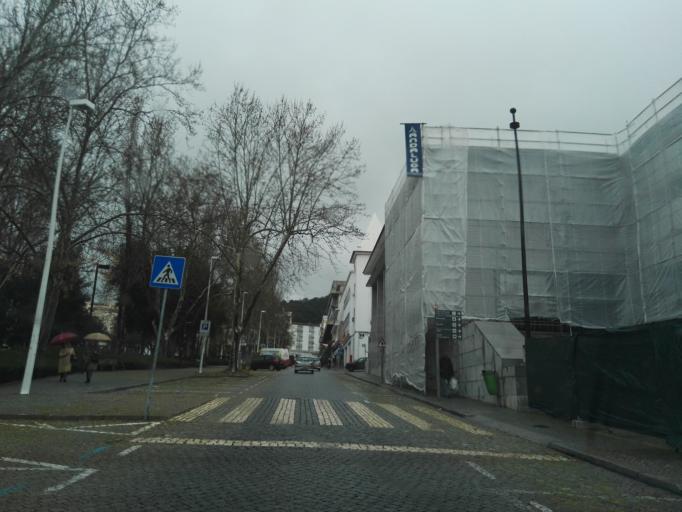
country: PT
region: Portalegre
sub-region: Portalegre
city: Portalegre
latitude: 39.2971
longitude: -7.4295
